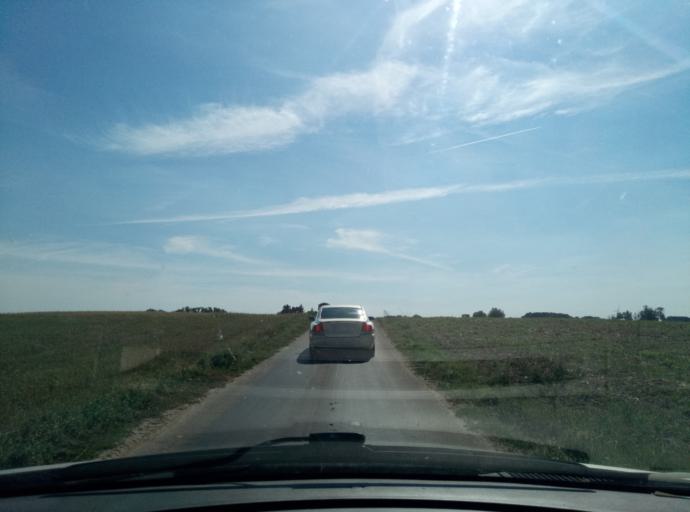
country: PL
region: Kujawsko-Pomorskie
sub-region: Powiat brodnicki
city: Jablonowo Pomorskie
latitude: 53.4068
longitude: 19.2388
